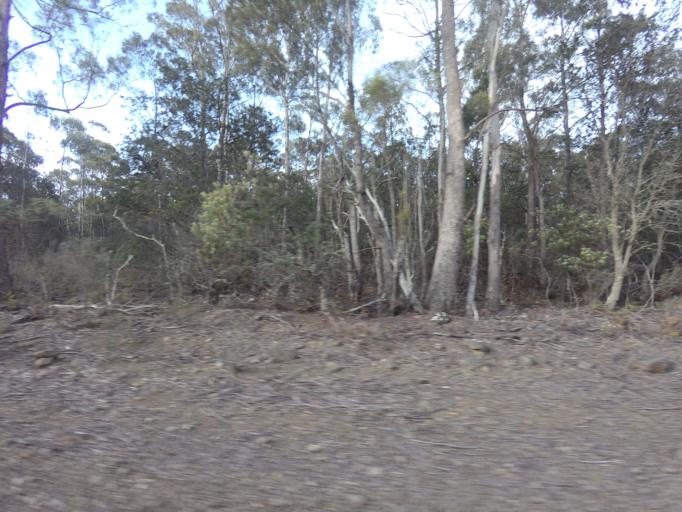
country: AU
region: Tasmania
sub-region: Break O'Day
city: St Helens
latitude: -41.8377
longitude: 148.0641
